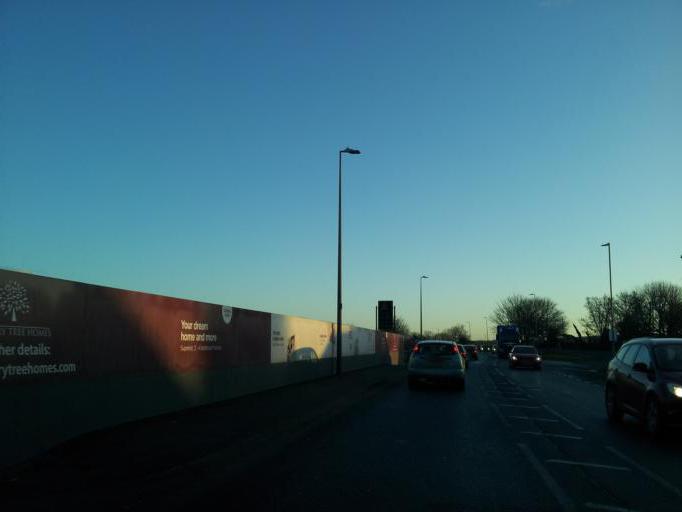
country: GB
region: England
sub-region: Lincolnshire
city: Sudbrooke
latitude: 53.2754
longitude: -0.4056
